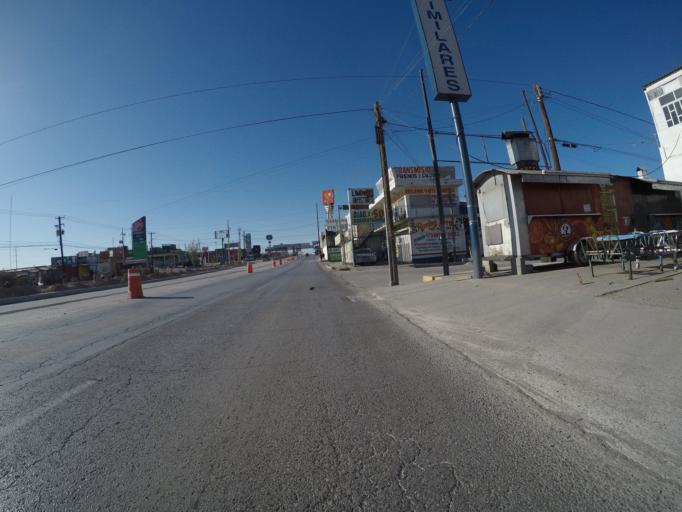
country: MX
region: Chihuahua
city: Ciudad Juarez
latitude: 31.6795
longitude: -106.4248
